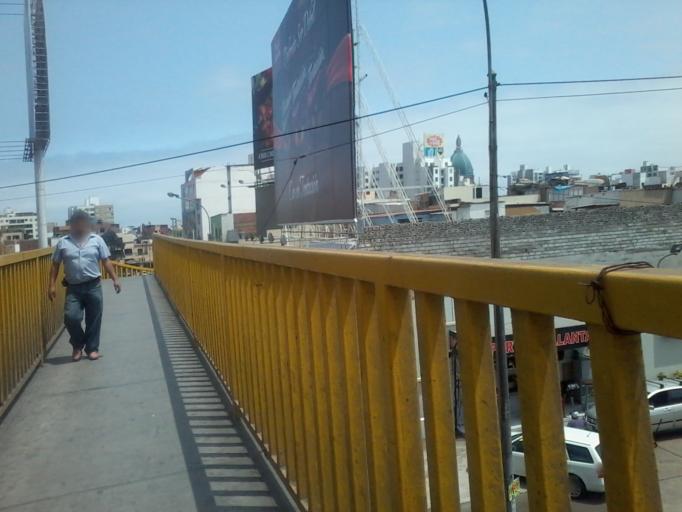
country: PE
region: Lima
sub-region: Lima
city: San Isidro
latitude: -12.0848
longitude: -77.0646
